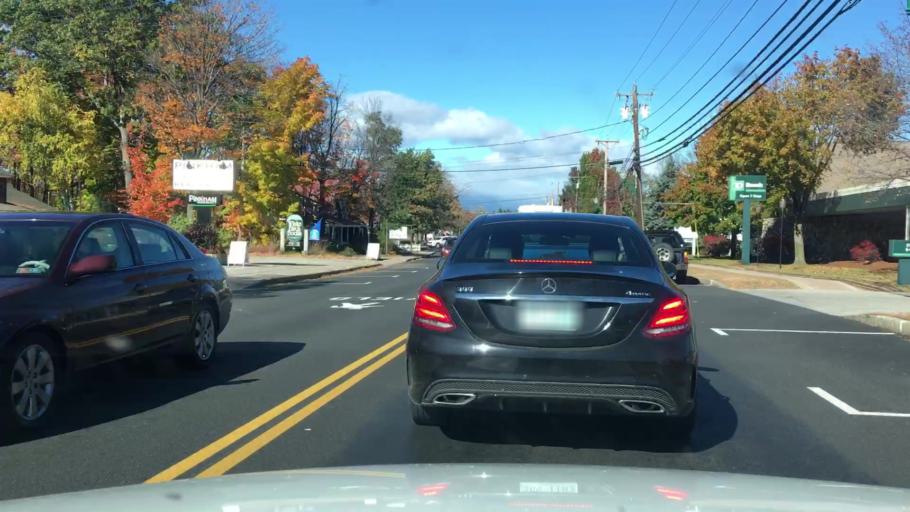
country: US
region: New Hampshire
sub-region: Carroll County
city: North Conway
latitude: 44.0495
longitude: -71.1252
